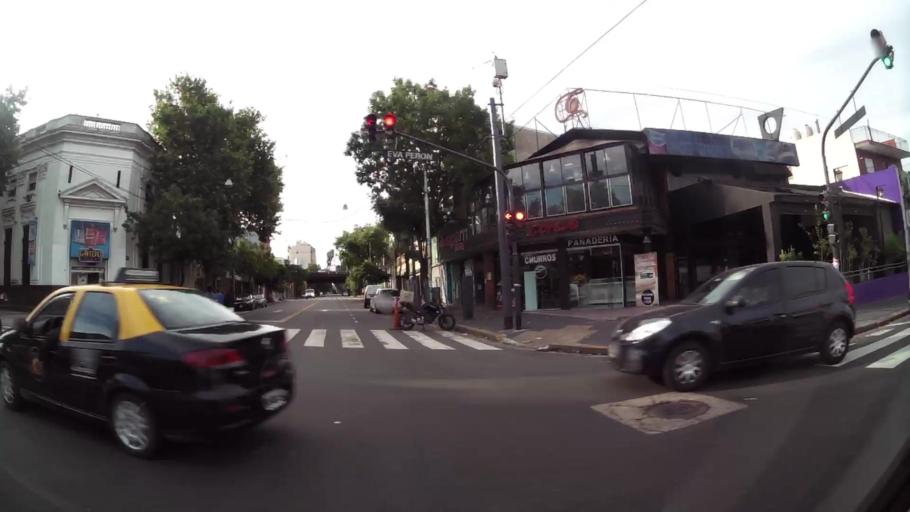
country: AR
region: Buenos Aires F.D.
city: Villa Santa Rita
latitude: -34.6411
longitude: -58.4569
